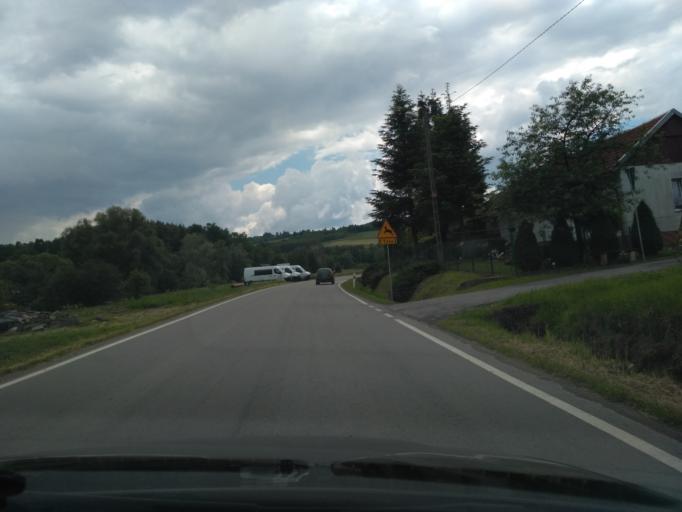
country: PL
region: Subcarpathian Voivodeship
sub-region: Powiat przeworski
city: Jawornik Polski
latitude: 49.9052
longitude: 22.3079
